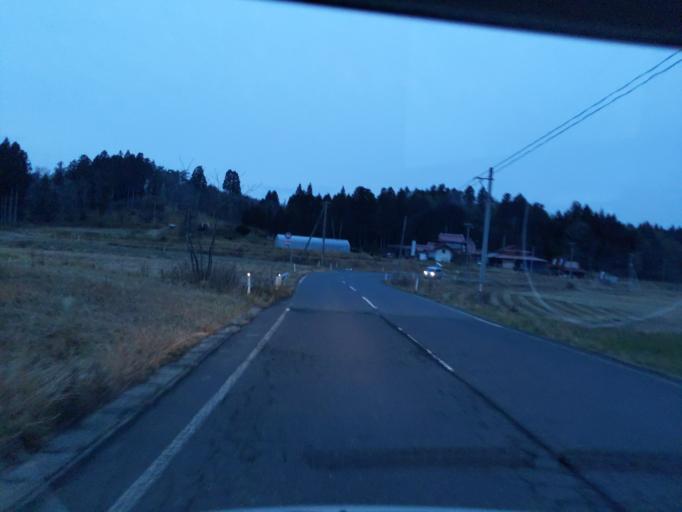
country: JP
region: Iwate
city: Ichinoseki
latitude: 38.8251
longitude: 141.1180
